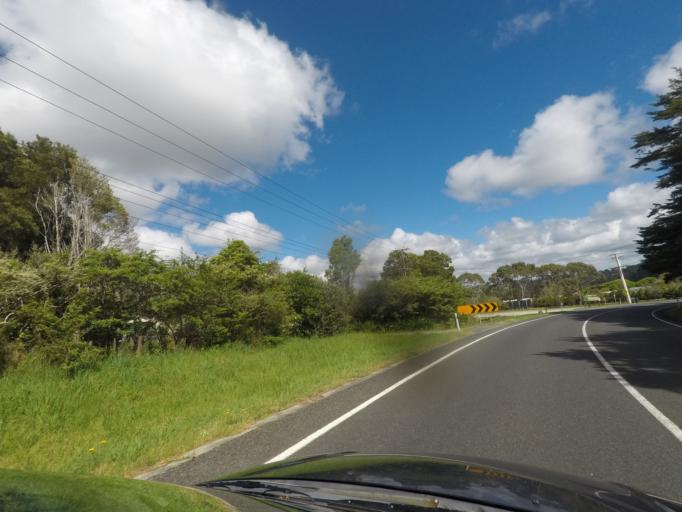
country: NZ
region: Auckland
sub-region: Auckland
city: Rothesay Bay
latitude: -36.7583
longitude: 174.6509
